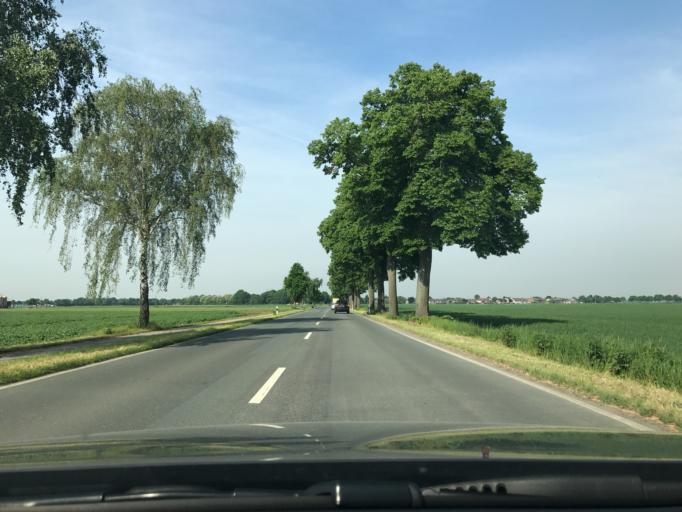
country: DE
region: North Rhine-Westphalia
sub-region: Regierungsbezirk Dusseldorf
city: Rheurdt
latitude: 51.4427
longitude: 6.4379
